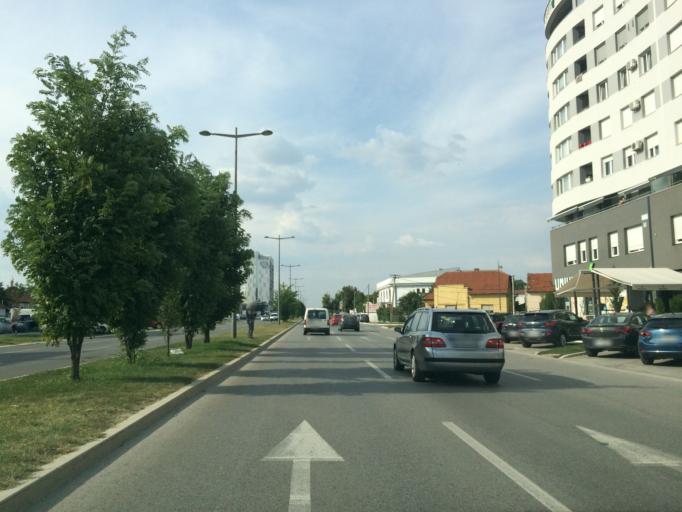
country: RS
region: Autonomna Pokrajina Vojvodina
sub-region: Juznobacki Okrug
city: Novi Sad
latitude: 45.2447
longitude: 19.8193
